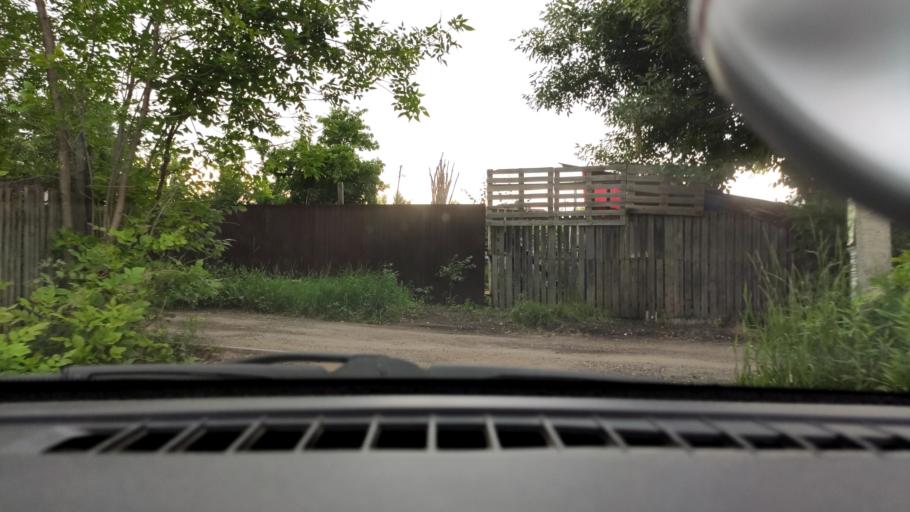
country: RU
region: Samara
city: Petra-Dubrava
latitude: 53.2651
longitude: 50.2903
